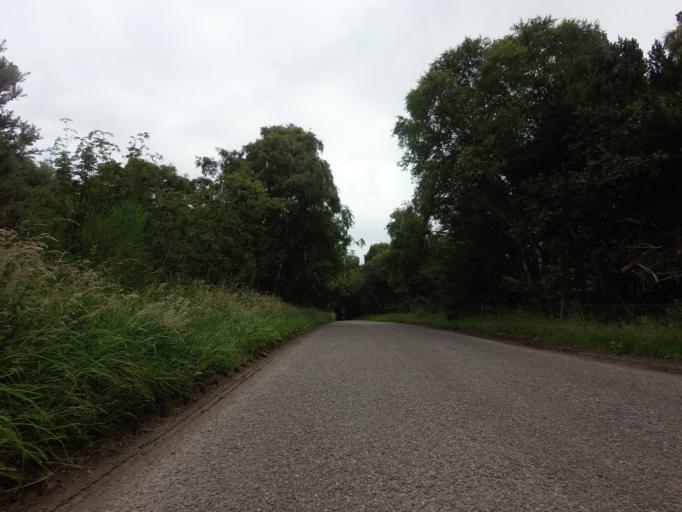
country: GB
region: Scotland
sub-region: Moray
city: Lhanbryd
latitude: 57.6636
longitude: -3.1778
